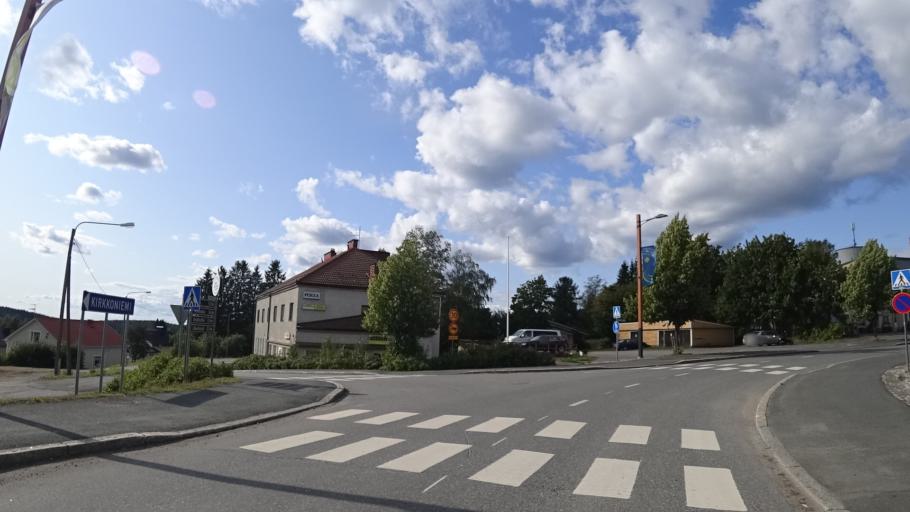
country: FI
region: North Karelia
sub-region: Keski-Karjala
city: Tohmajaervi
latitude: 62.2239
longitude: 30.3297
